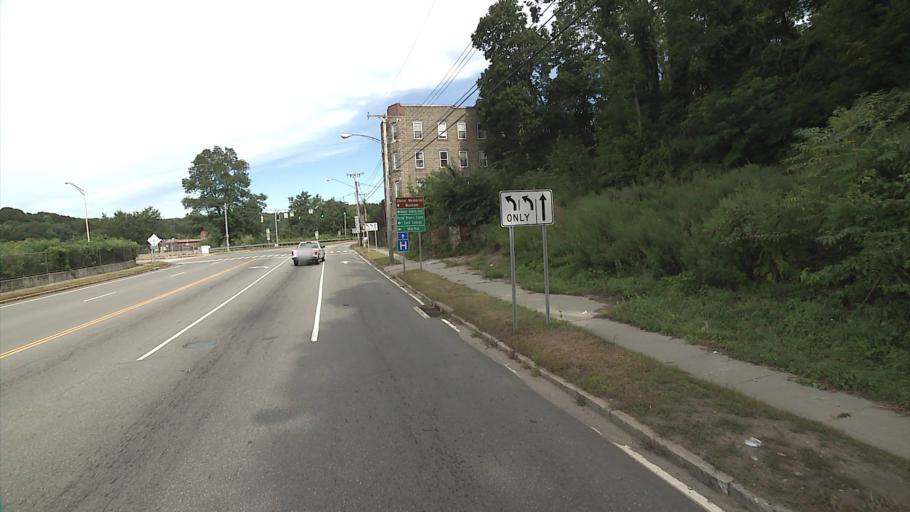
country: US
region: Connecticut
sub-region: New London County
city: Norwich
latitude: 41.5252
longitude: -72.0807
